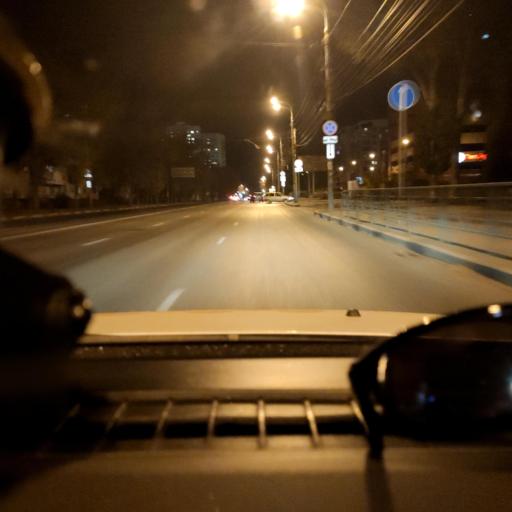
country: RU
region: Samara
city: Samara
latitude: 53.2094
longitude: 50.1894
